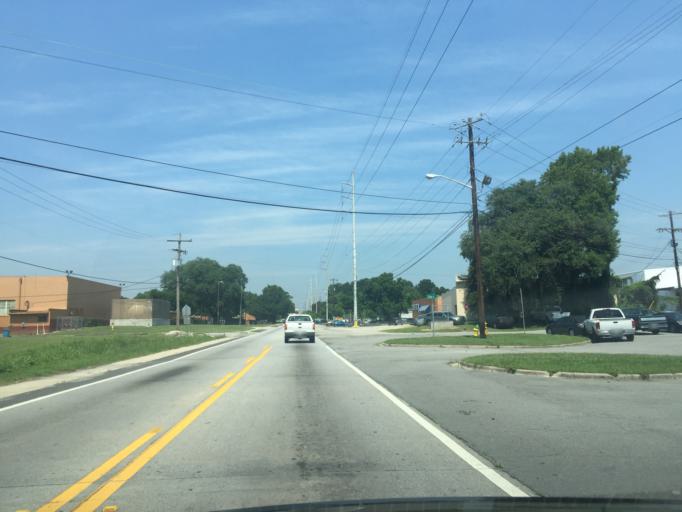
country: US
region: Georgia
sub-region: Chatham County
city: Savannah
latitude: 32.0498
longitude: -81.1204
